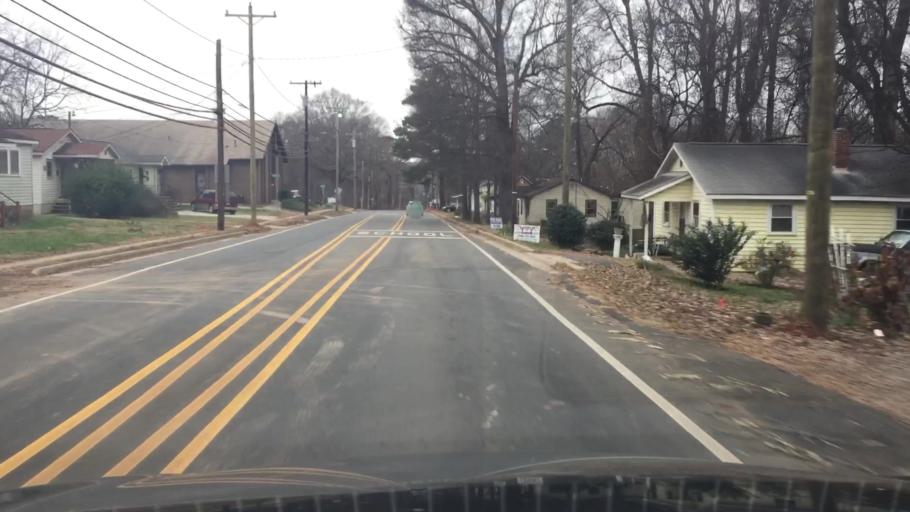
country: US
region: North Carolina
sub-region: Iredell County
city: Mooresville
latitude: 35.5873
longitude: -80.8214
